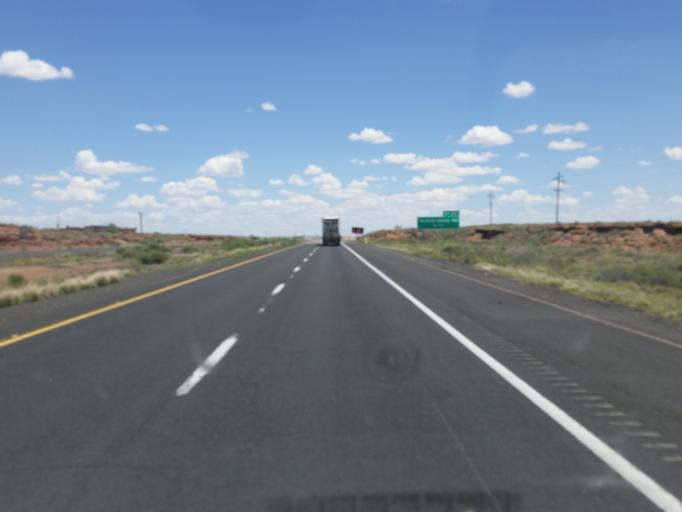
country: US
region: Arizona
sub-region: Navajo County
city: Holbrook
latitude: 34.9091
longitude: -110.2288
